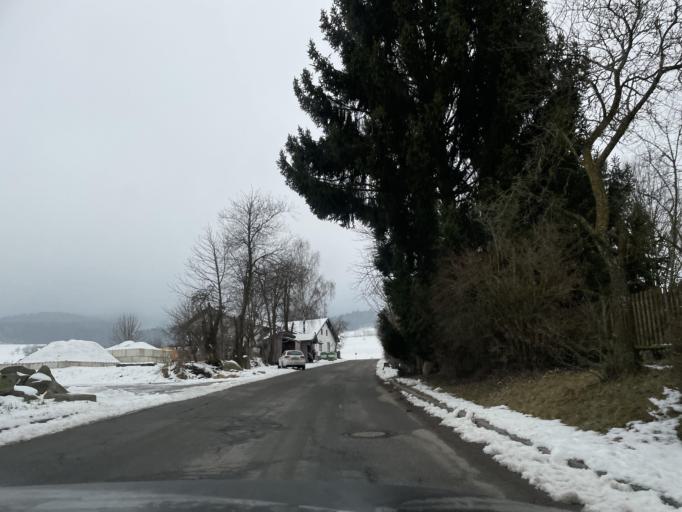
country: DE
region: Bavaria
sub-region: Lower Bavaria
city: Kollnburg
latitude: 49.0225
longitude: 12.8845
